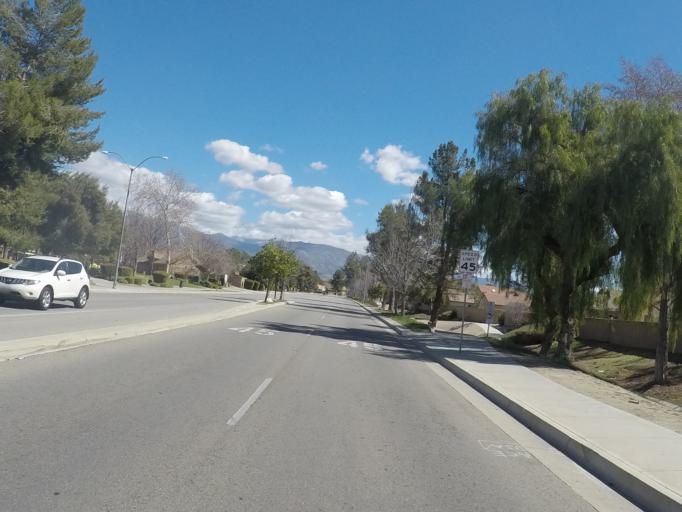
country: US
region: California
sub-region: Riverside County
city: San Jacinto
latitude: 33.7723
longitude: -116.9455
